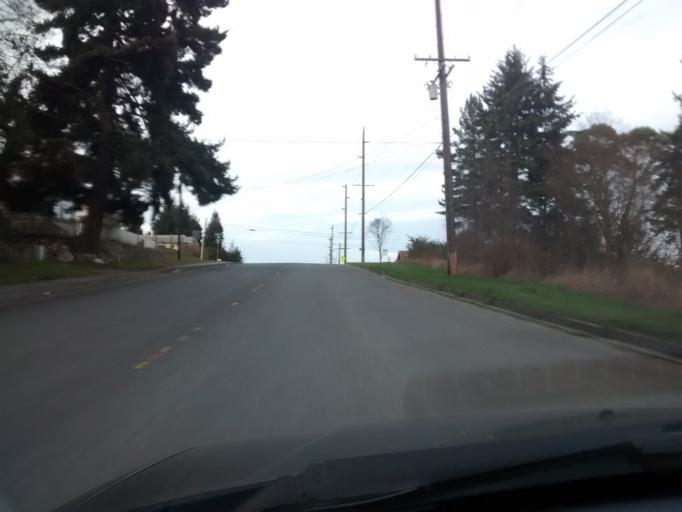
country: US
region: Washington
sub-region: Clallam County
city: Port Angeles
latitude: 48.1245
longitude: -123.4696
